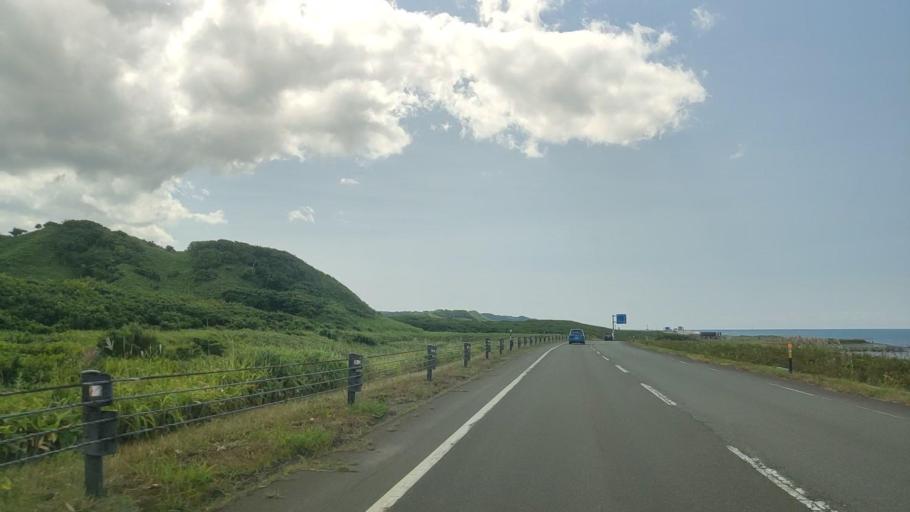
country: JP
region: Hokkaido
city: Wakkanai
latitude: 45.2690
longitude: 141.6091
